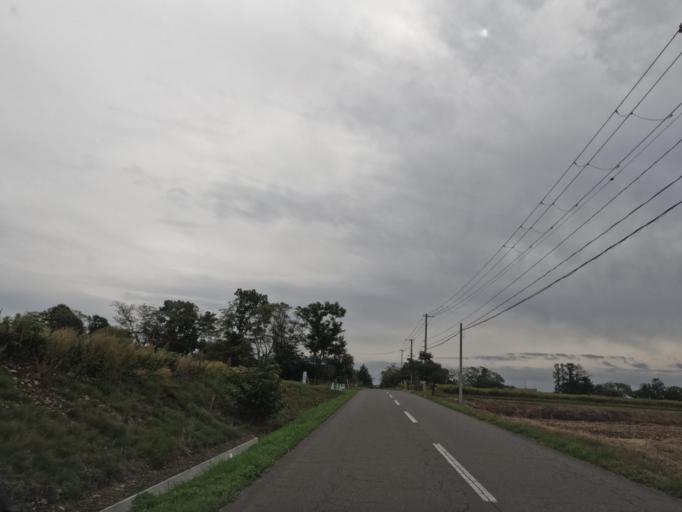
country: JP
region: Hokkaido
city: Date
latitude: 42.4345
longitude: 140.9085
